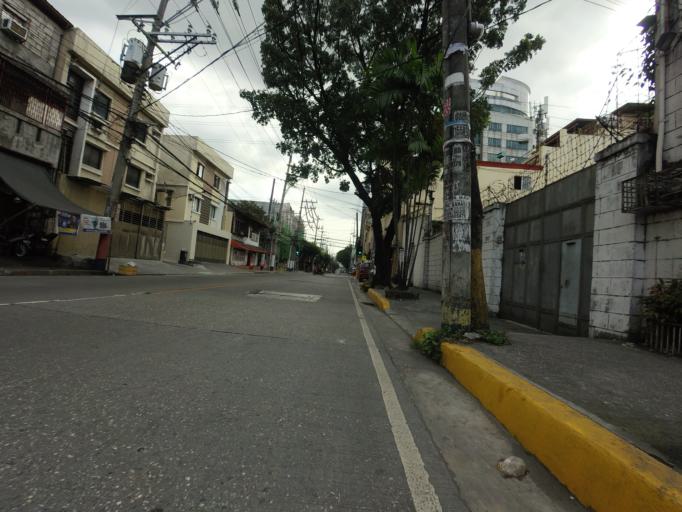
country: PH
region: Metro Manila
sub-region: City of Manila
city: Quiapo
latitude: 14.5821
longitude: 120.9972
